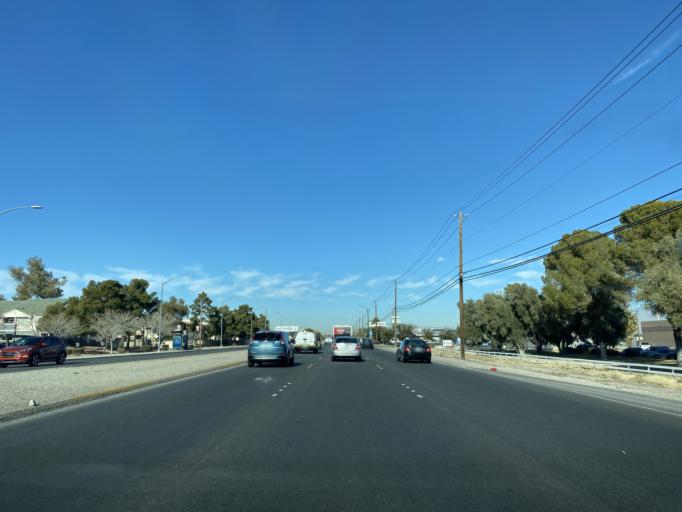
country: US
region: Nevada
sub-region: Clark County
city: Las Vegas
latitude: 36.2266
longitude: -115.2206
